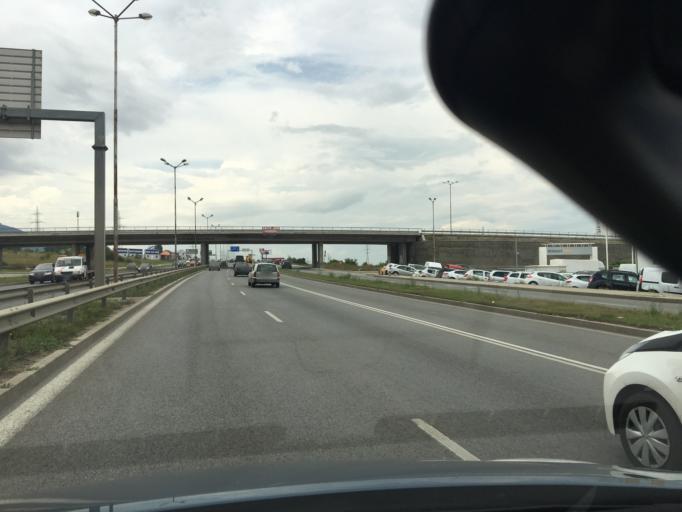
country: BG
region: Sofia-Capital
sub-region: Stolichna Obshtina
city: Sofia
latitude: 42.6254
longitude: 23.3526
